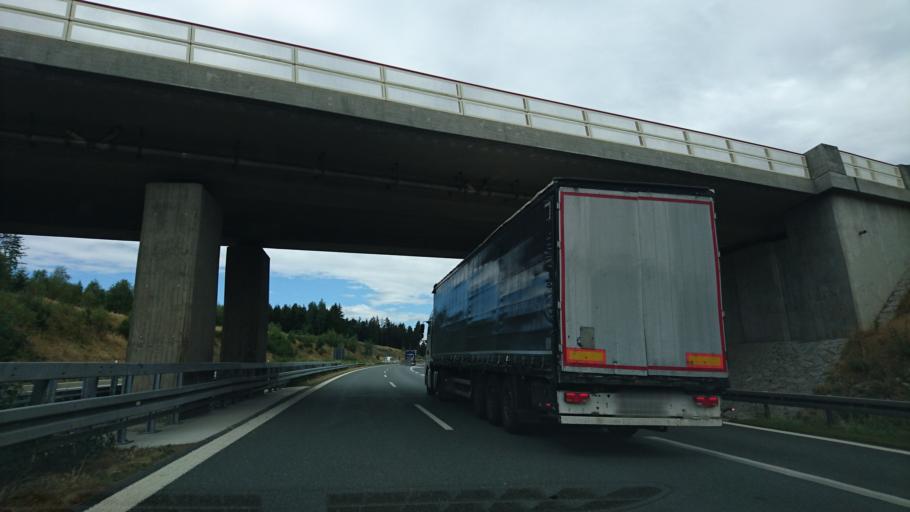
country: DE
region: Bavaria
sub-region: Upper Franconia
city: Trogen
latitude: 50.3518
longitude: 11.9724
